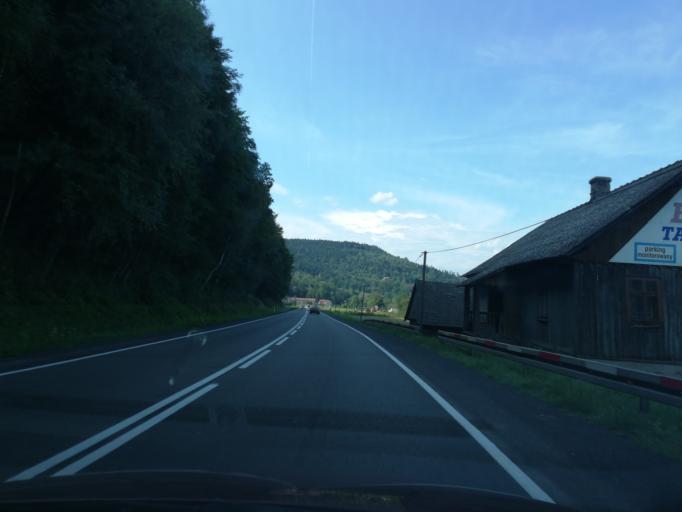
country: PL
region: Lesser Poland Voivodeship
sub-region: Powiat nowosadecki
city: Lososina Dolna
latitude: 49.7727
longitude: 20.6434
